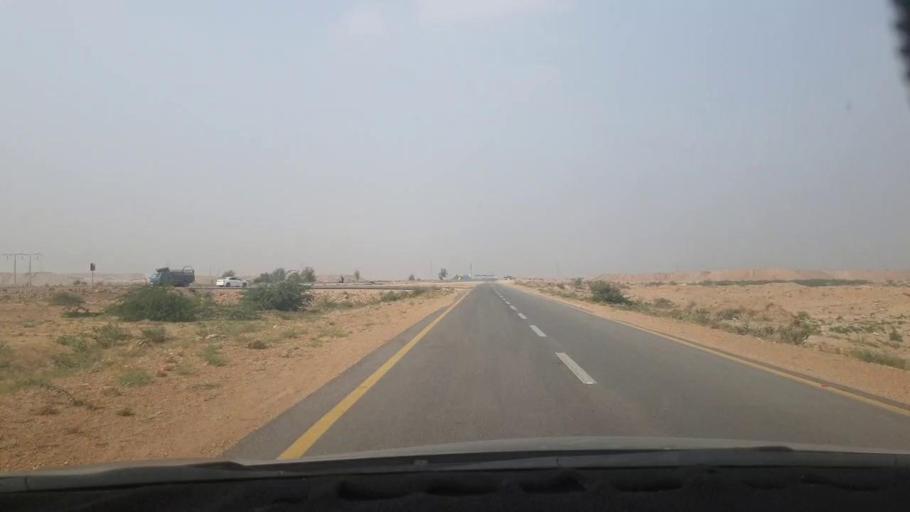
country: PK
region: Sindh
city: Matiari
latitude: 25.5717
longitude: 68.3152
